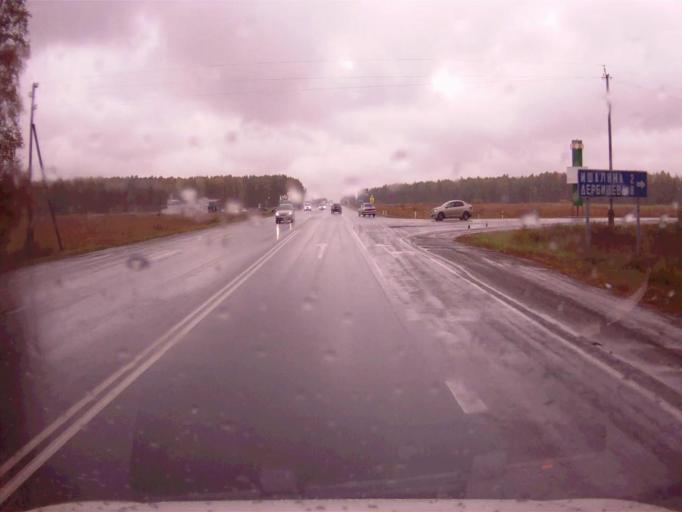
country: RU
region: Chelyabinsk
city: Argayash
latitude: 55.4160
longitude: 61.0288
